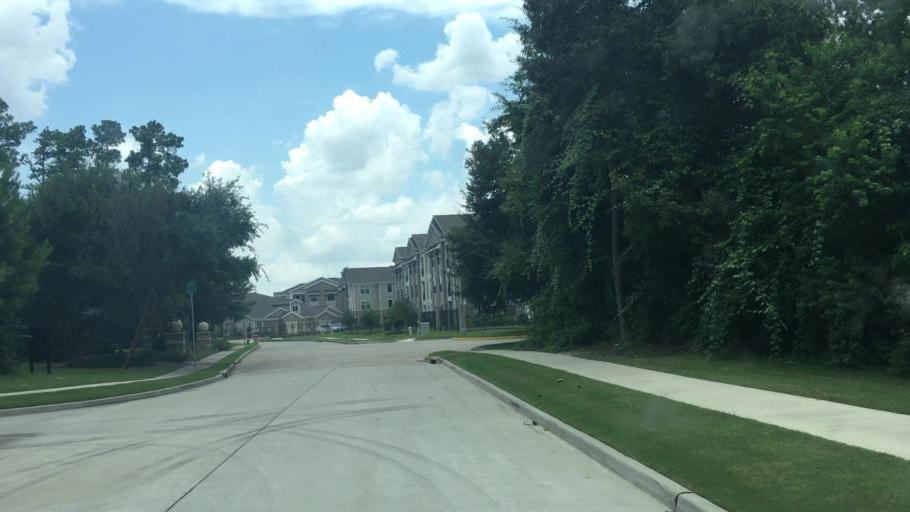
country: US
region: Texas
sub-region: Harris County
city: Atascocita
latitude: 29.9884
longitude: -95.1886
